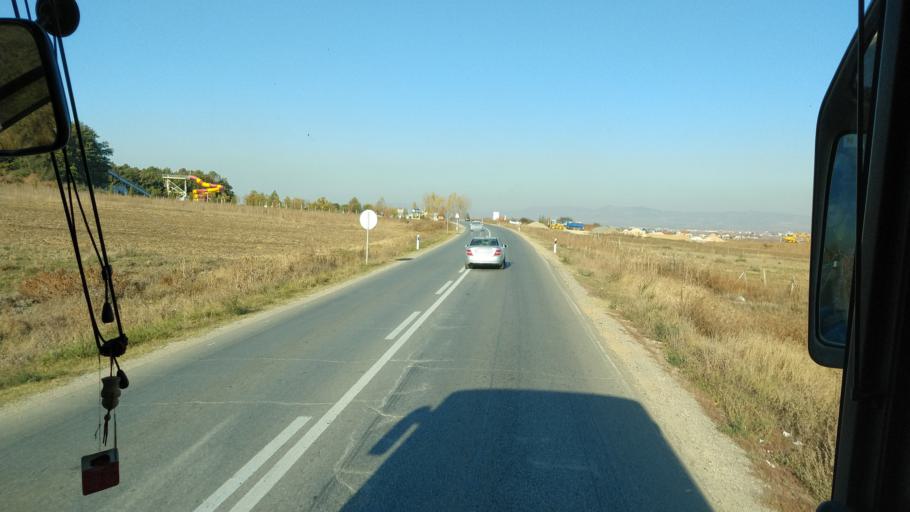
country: XK
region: Pristina
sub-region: Lipjan
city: Lipljan
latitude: 42.4982
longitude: 21.1066
